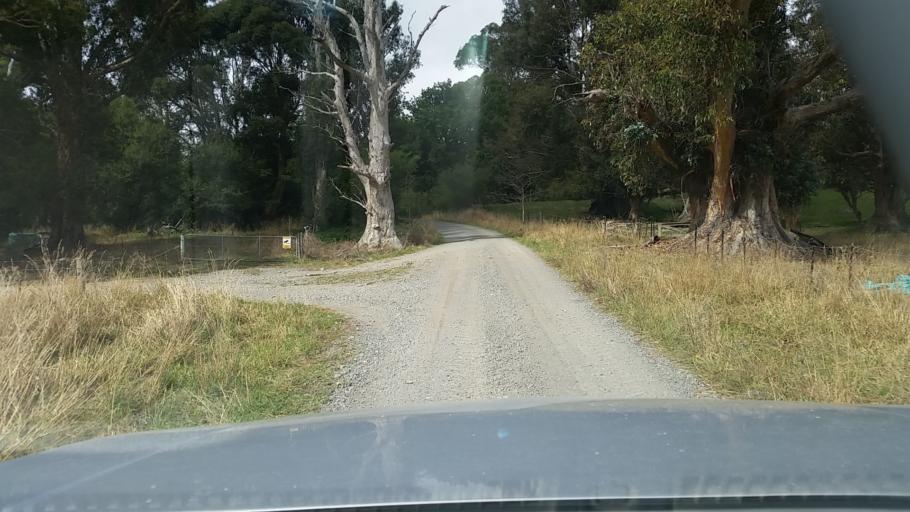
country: NZ
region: Marlborough
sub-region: Marlborough District
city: Blenheim
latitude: -41.7360
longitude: 173.8913
